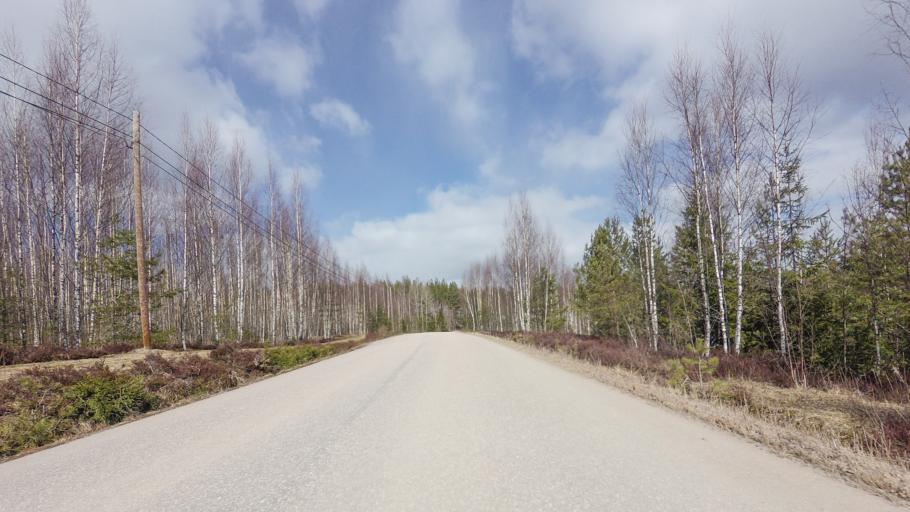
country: FI
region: Varsinais-Suomi
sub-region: Salo
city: Suomusjaervi
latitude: 60.3114
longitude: 23.6425
